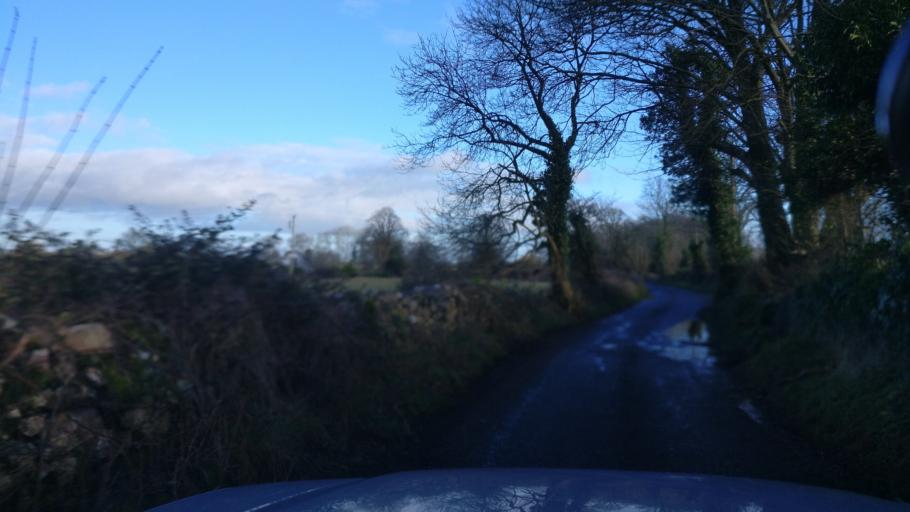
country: IE
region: Connaught
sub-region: County Galway
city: Loughrea
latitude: 53.2297
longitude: -8.5722
